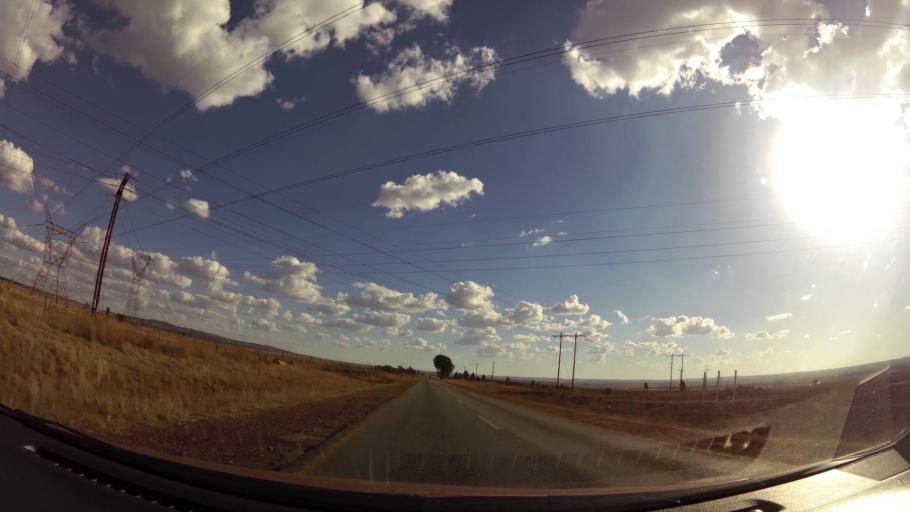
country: ZA
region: Gauteng
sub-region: West Rand District Municipality
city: Carletonville
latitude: -26.3975
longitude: 27.3037
